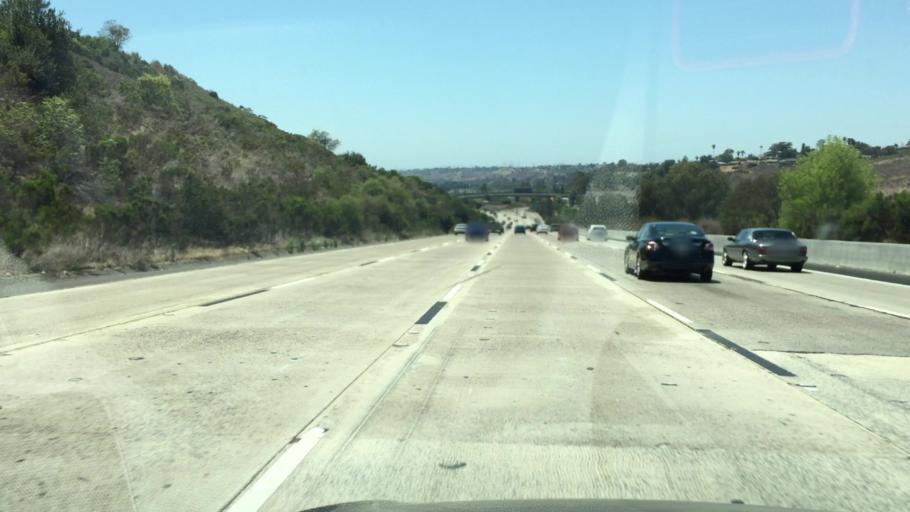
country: US
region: California
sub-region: San Diego County
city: La Mesa
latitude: 32.7800
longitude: -117.0787
